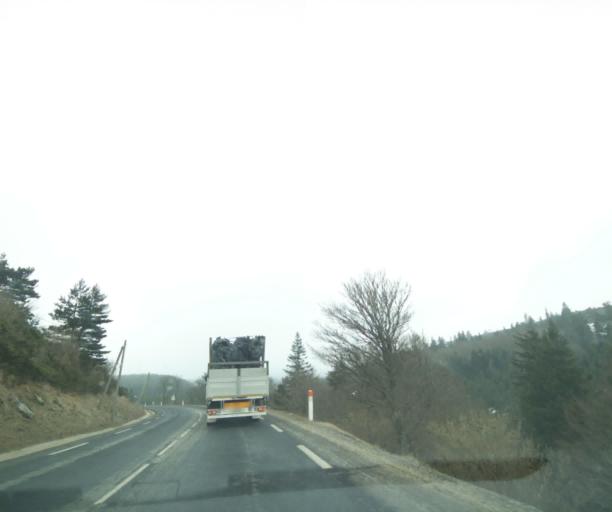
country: FR
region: Languedoc-Roussillon
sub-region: Departement de la Lozere
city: Langogne
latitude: 44.7133
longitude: 4.0072
